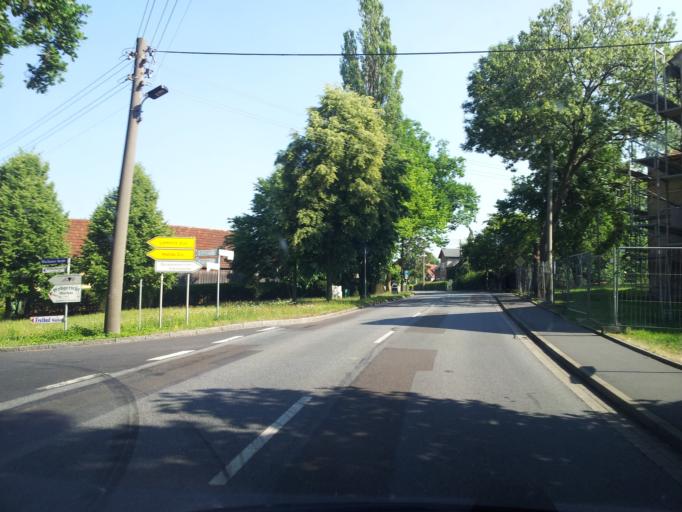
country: DE
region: Saxony
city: Wachau
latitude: 51.1586
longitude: 13.8837
